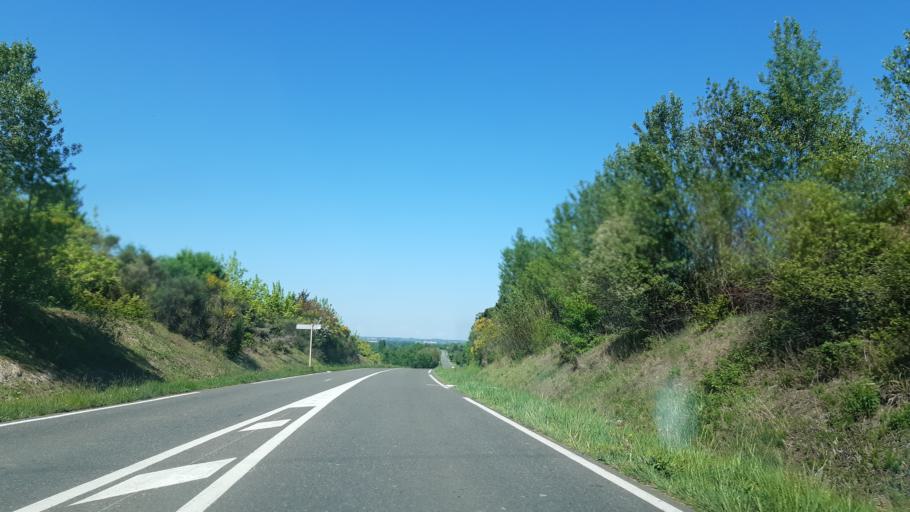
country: FR
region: Midi-Pyrenees
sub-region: Departement du Gers
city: Pujaudran
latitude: 43.5812
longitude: 1.0450
